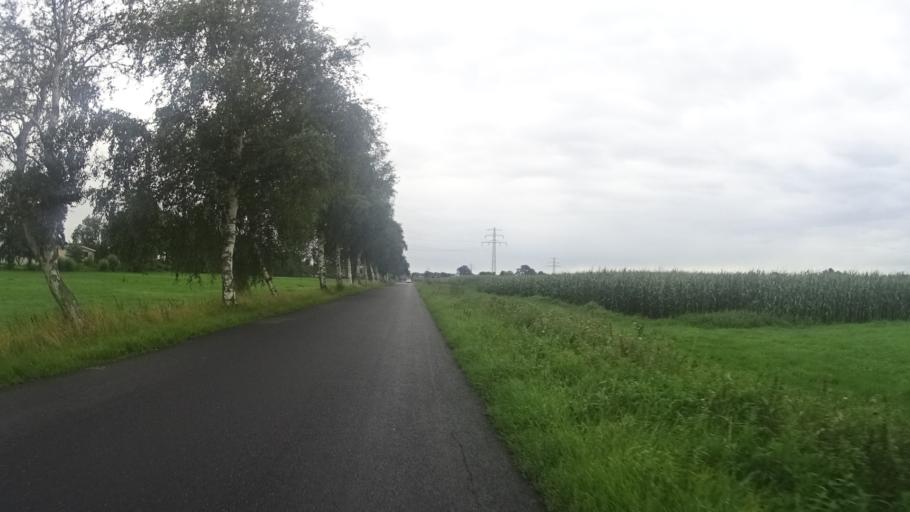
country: DE
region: Schleswig-Holstein
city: Kiebitzreihe
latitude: 53.7874
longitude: 9.6045
